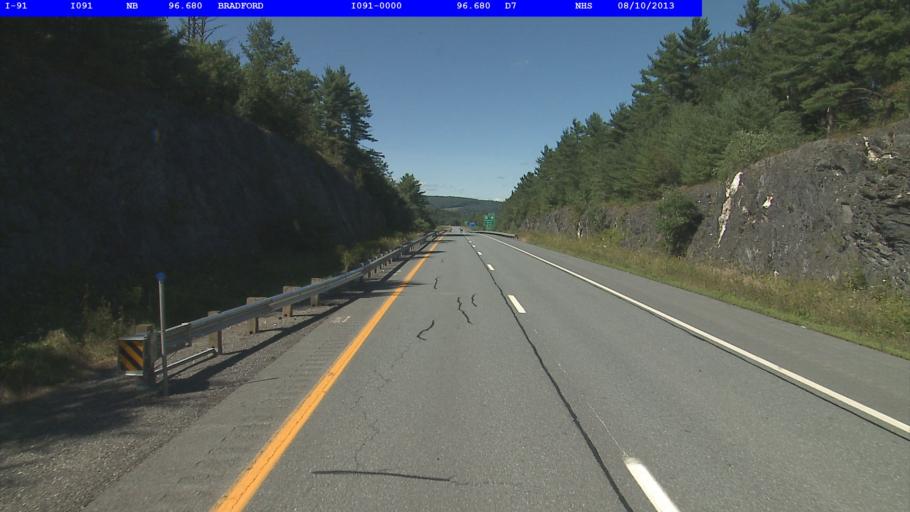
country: US
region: New Hampshire
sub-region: Grafton County
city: Orford
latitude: 43.9714
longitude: -72.1255
